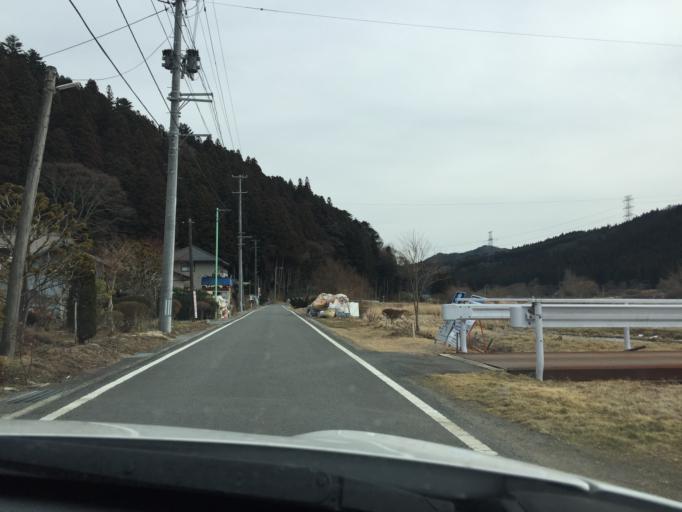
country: JP
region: Fukushima
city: Iwaki
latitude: 37.1424
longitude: 140.6914
